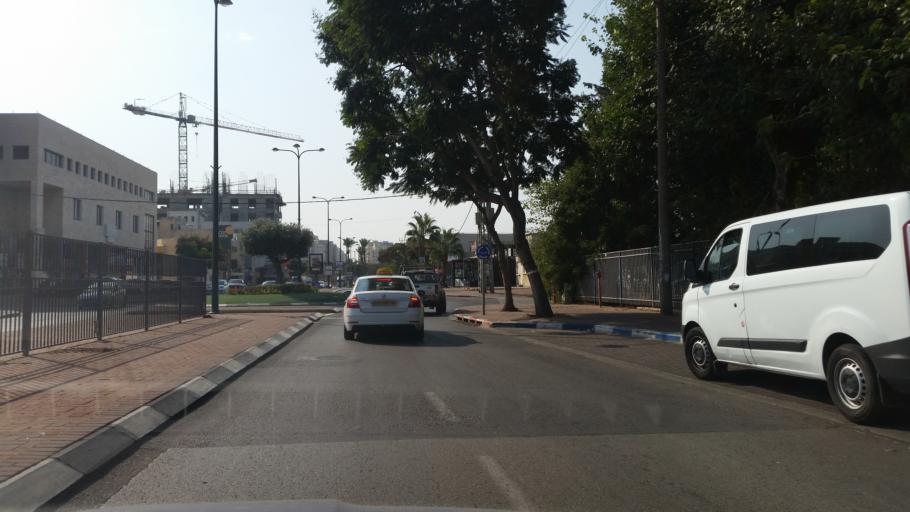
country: IL
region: Central District
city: Bet Yizhaq
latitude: 32.3158
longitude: 34.8737
